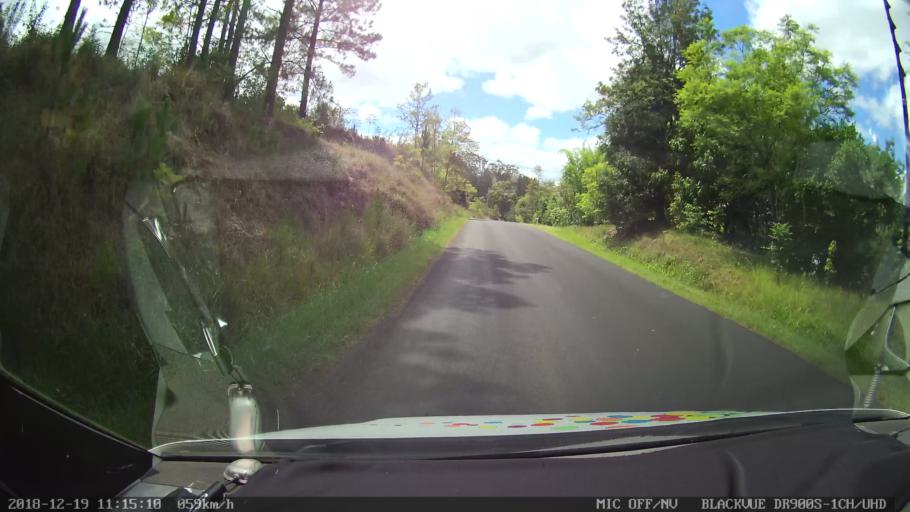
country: AU
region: New South Wales
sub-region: Lismore Municipality
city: Nimbin
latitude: -28.6657
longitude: 153.2766
